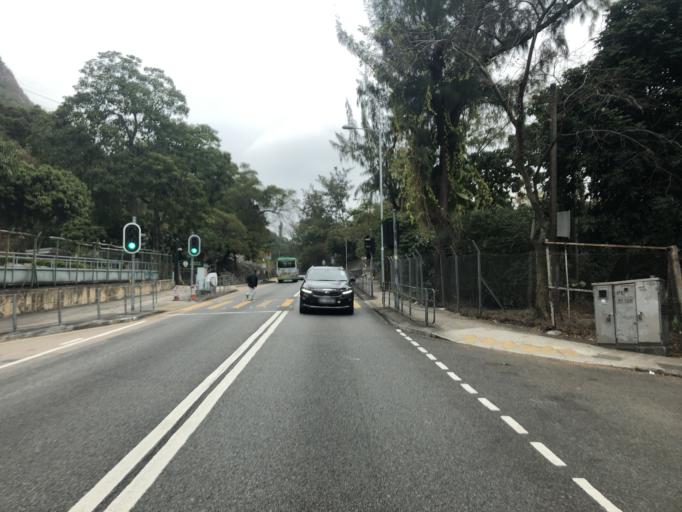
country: HK
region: Wong Tai Sin
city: Wong Tai Sin
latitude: 22.3338
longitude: 114.2207
